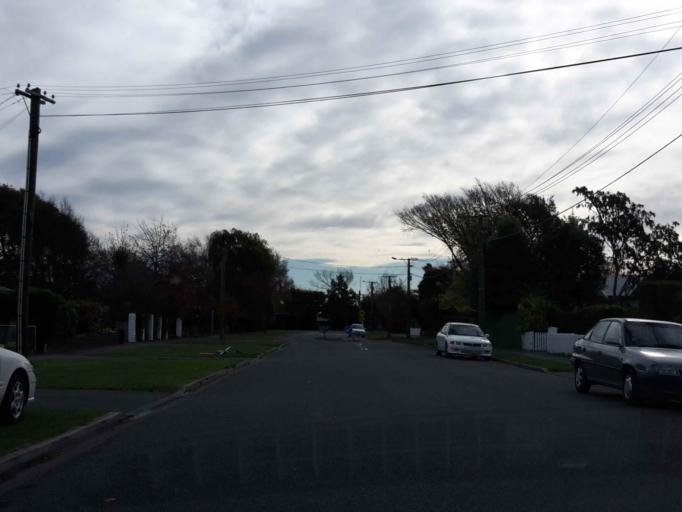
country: NZ
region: Canterbury
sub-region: Christchurch City
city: Christchurch
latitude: -43.5673
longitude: 172.6211
